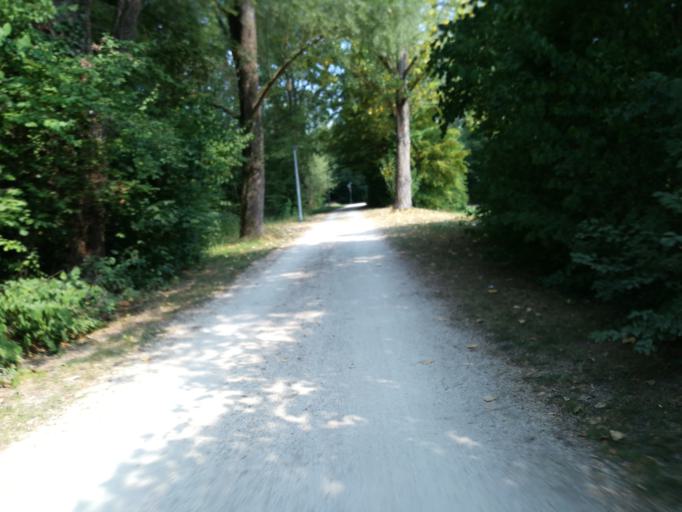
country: DE
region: Baden-Wuerttemberg
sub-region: Freiburg Region
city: Singen
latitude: 47.7702
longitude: 8.8247
